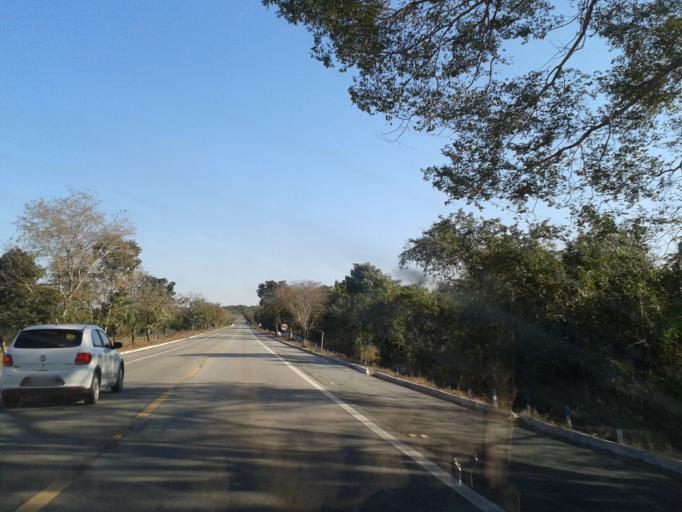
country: BR
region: Goias
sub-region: Mozarlandia
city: Mozarlandia
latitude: -15.1417
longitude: -50.5871
